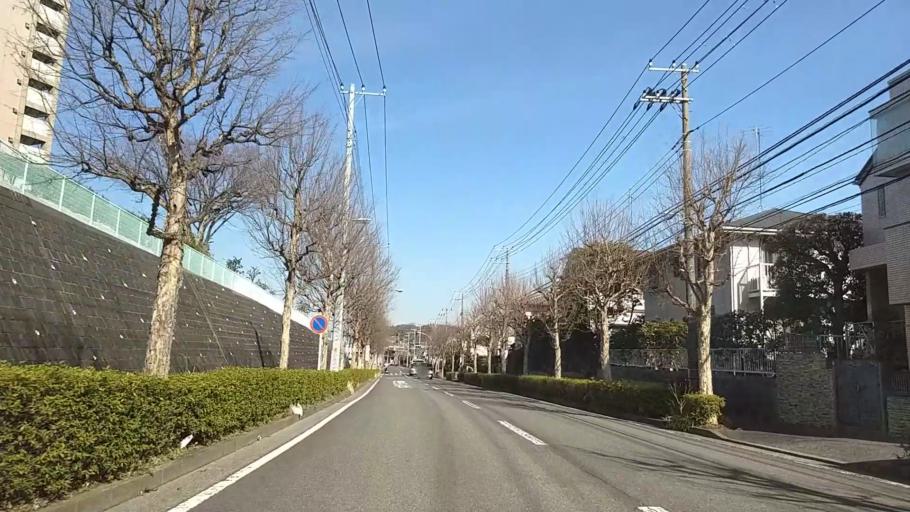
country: JP
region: Kanagawa
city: Kamakura
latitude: 35.3776
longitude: 139.5850
